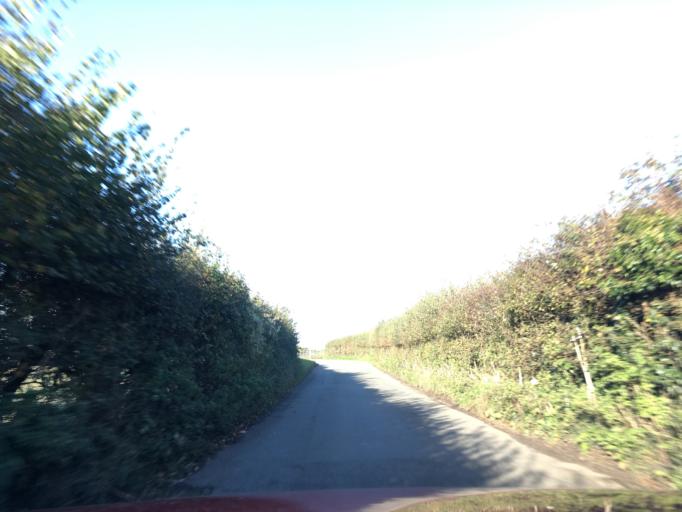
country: GB
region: England
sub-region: South Gloucestershire
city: Thornbury
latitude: 51.6223
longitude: -2.5099
